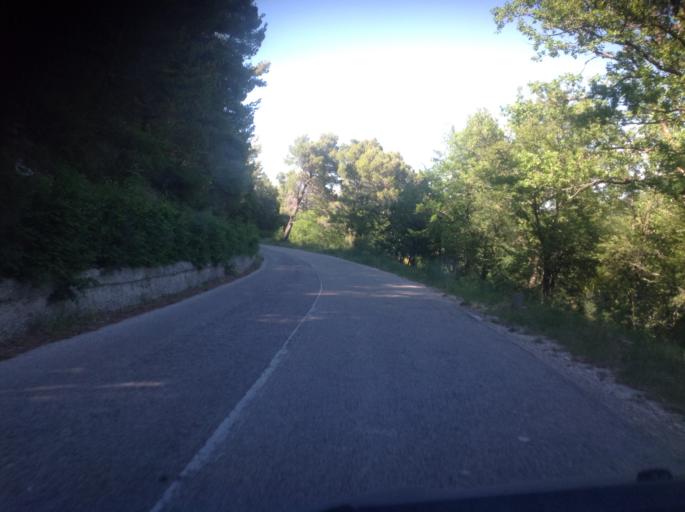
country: IT
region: Umbria
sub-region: Provincia di Terni
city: Stroncone
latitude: 42.4801
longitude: 12.6694
